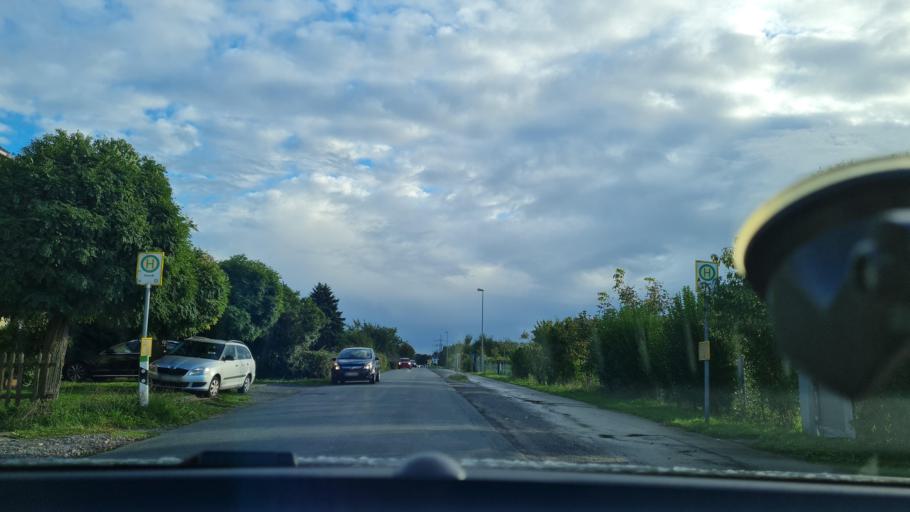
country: DE
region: North Rhine-Westphalia
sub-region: Regierungsbezirk Dusseldorf
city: Dinslaken
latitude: 51.5527
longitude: 6.7683
